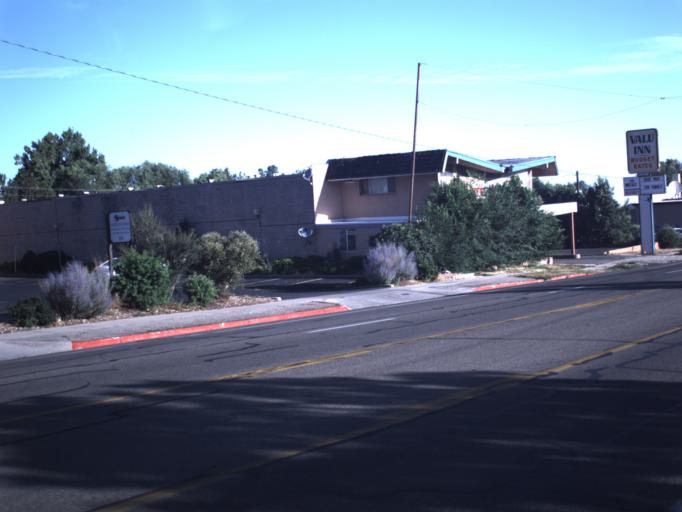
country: US
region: Utah
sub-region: Iron County
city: Cedar City
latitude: 37.6709
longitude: -113.0616
